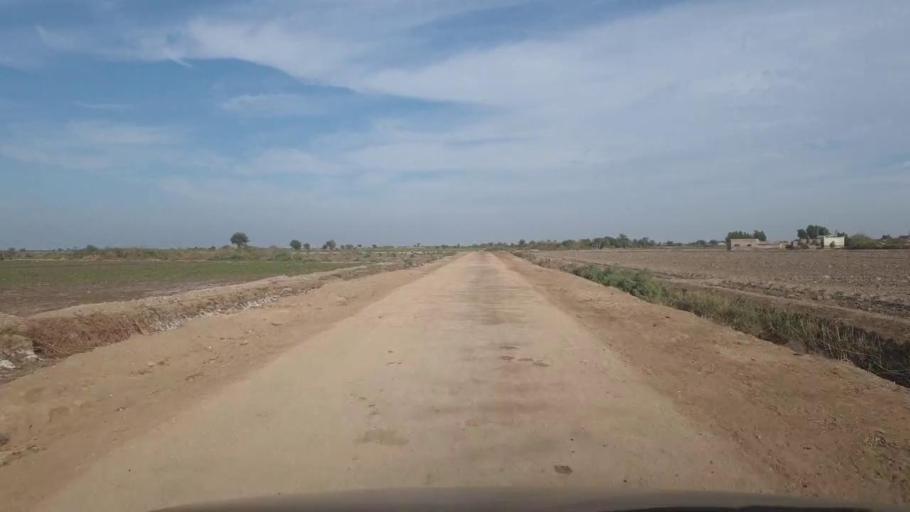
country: PK
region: Sindh
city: Mirwah Gorchani
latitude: 25.3616
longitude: 69.2130
